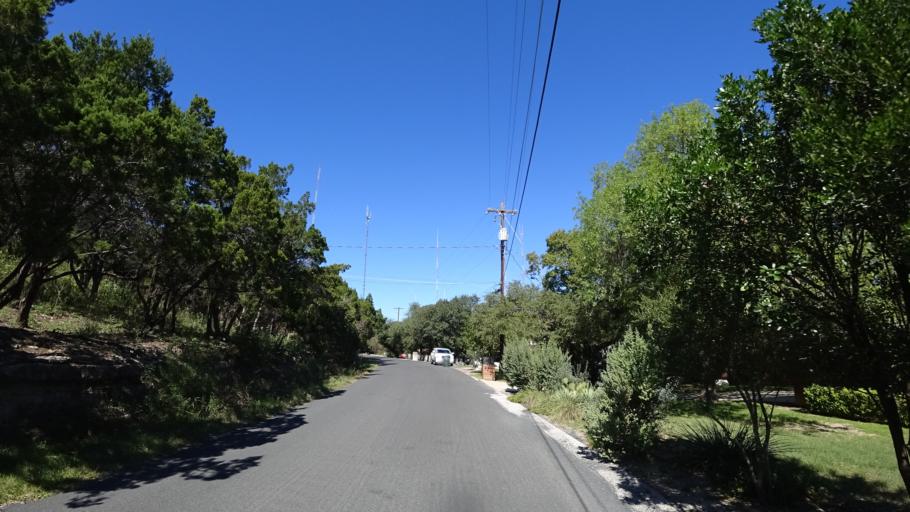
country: US
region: Texas
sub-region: Travis County
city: West Lake Hills
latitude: 30.3157
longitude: -97.7963
